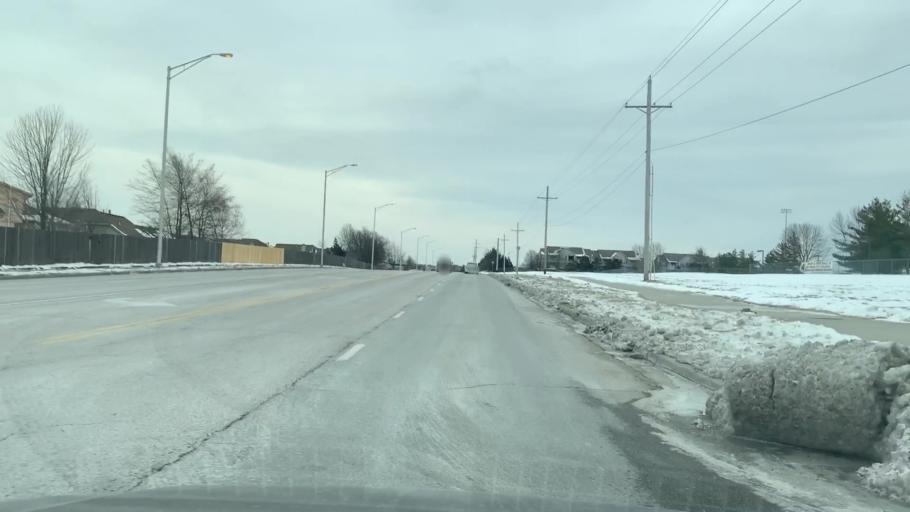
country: US
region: Missouri
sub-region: Jackson County
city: Lees Summit
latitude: 38.9304
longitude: -94.3739
